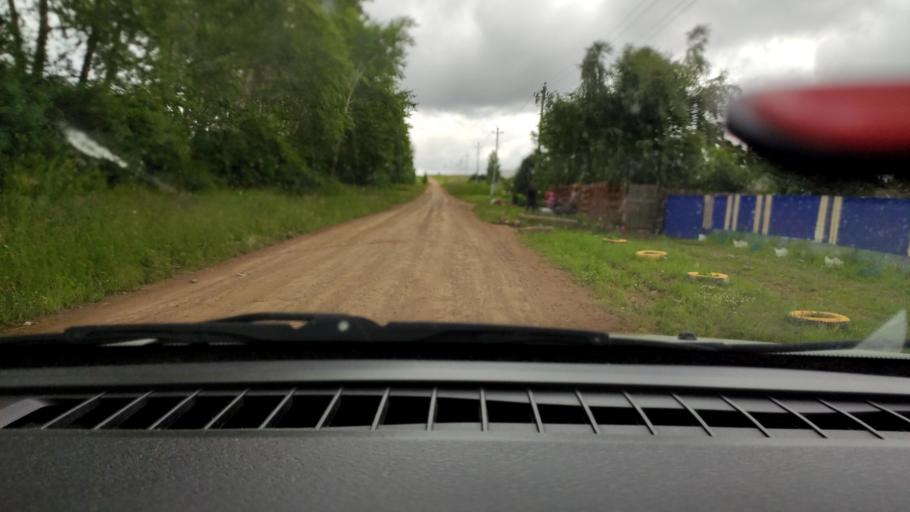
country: RU
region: Perm
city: Chaykovskaya
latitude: 58.1441
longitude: 55.5744
